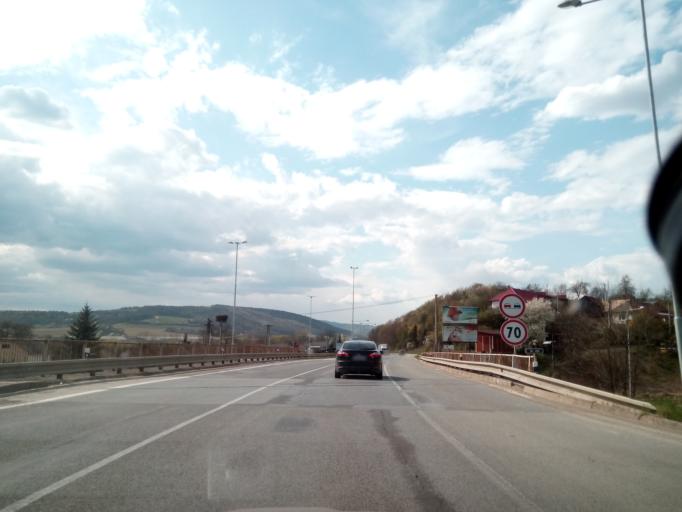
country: SK
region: Presovsky
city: Sabinov
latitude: 49.0038
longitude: 21.0781
